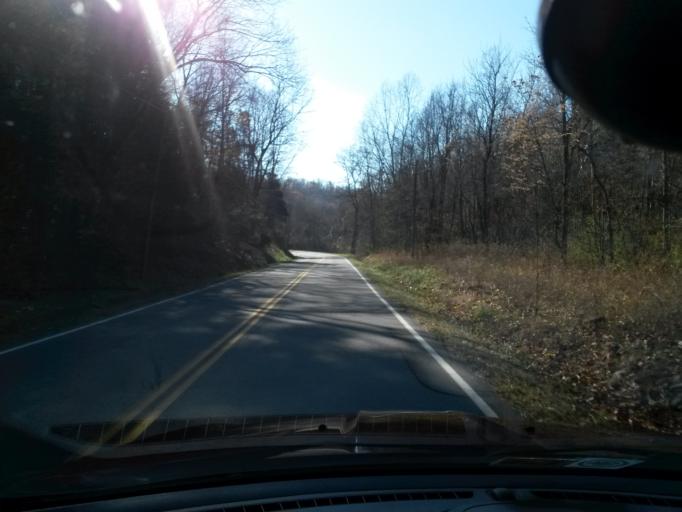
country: US
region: Virginia
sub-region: Botetourt County
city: Buchanan
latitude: 37.6236
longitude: -79.7351
